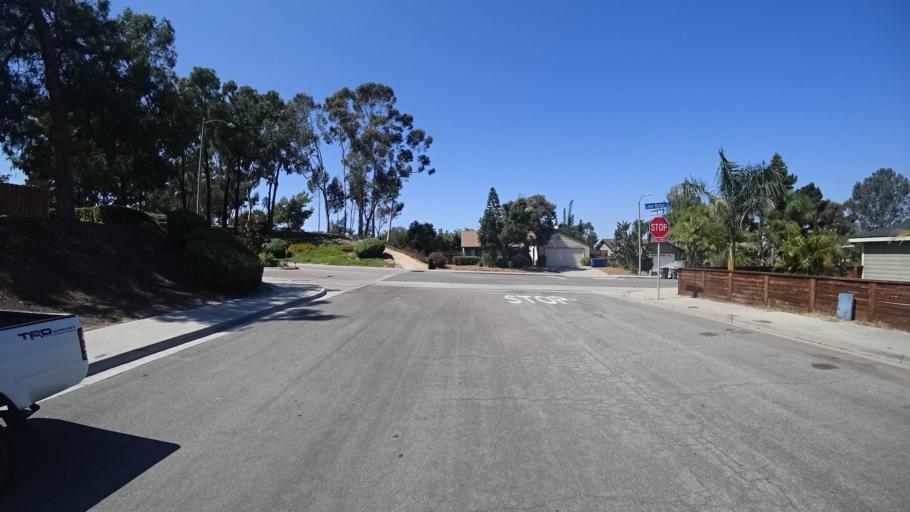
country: US
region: California
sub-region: San Diego County
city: Lake San Marcos
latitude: 33.1262
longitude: -117.2174
